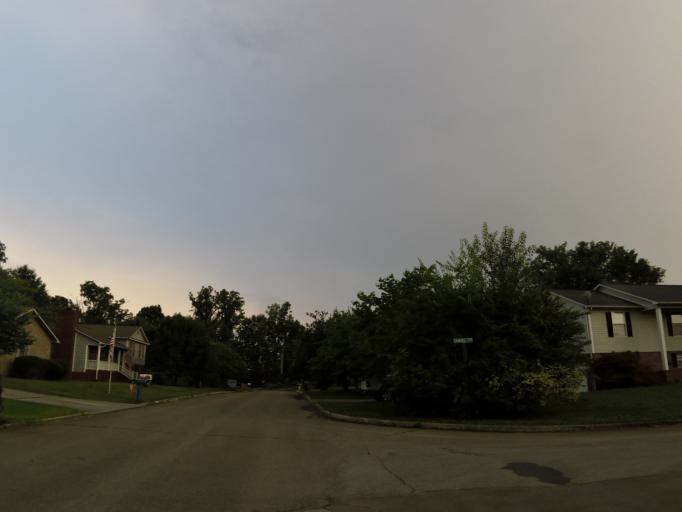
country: US
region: Tennessee
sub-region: Blount County
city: Wildwood
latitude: 35.8027
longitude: -83.8827
